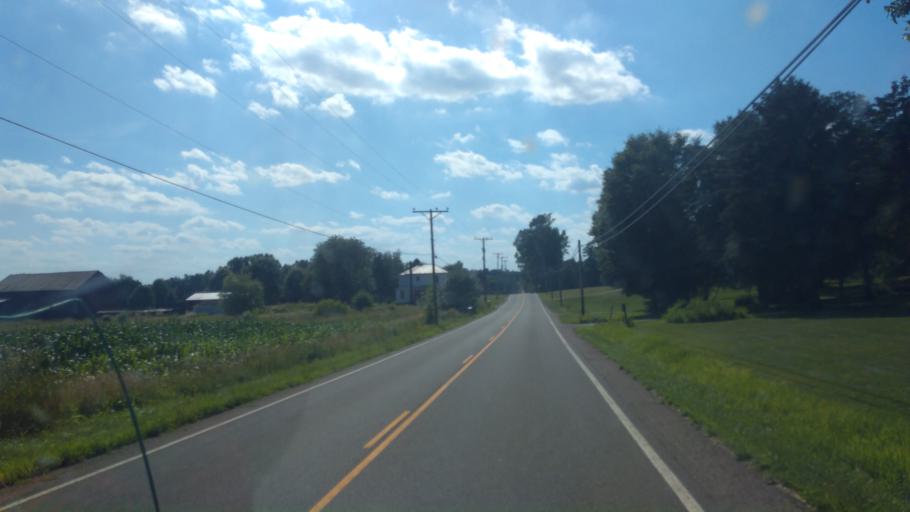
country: US
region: Ohio
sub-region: Stark County
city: Navarre
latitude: 40.7264
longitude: -81.5546
